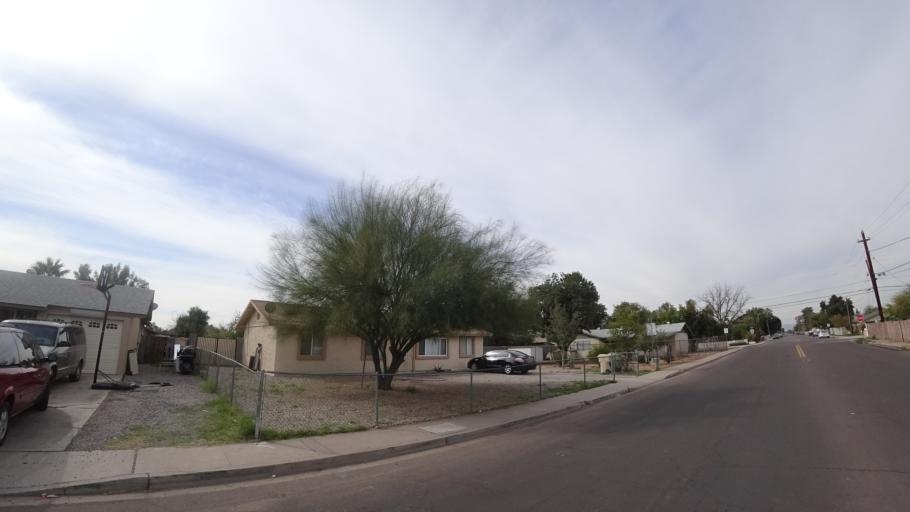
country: US
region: Arizona
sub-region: Maricopa County
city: Glendale
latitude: 33.5348
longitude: -112.1942
